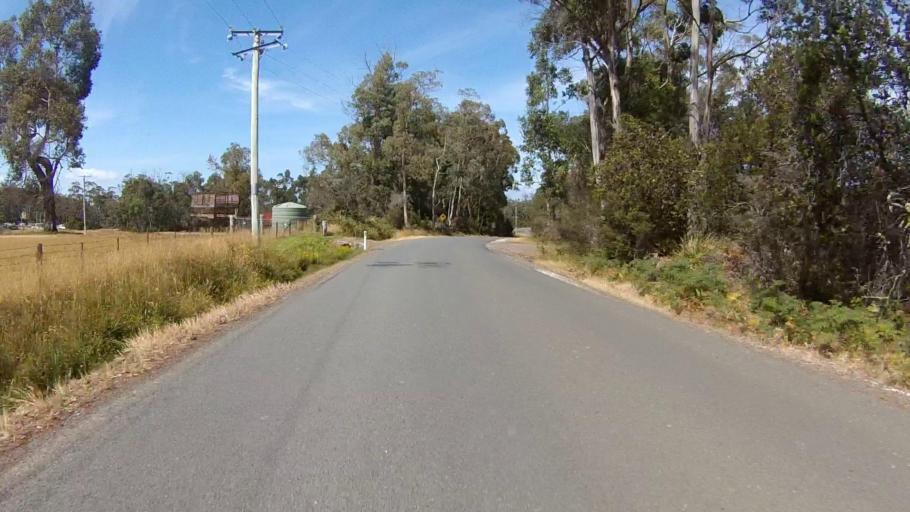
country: AU
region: Tasmania
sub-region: Huon Valley
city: Cygnet
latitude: -43.2387
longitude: 147.1247
